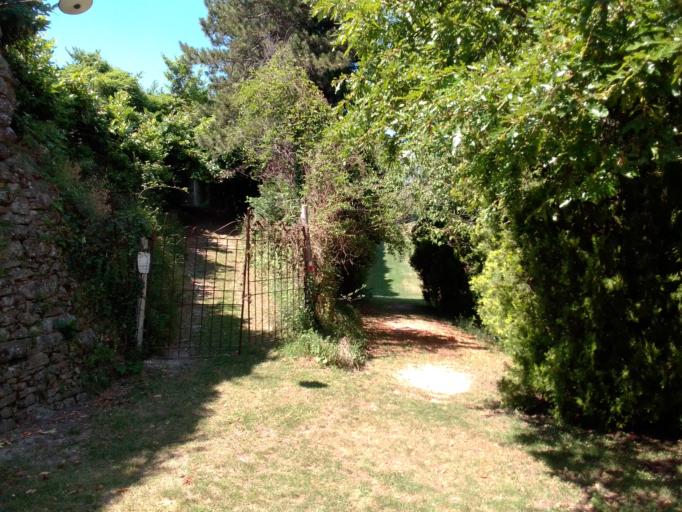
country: IT
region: Emilia-Romagna
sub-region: Provincia di Piacenza
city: Pianello Val Tidone
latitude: 44.9134
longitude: 9.3940
